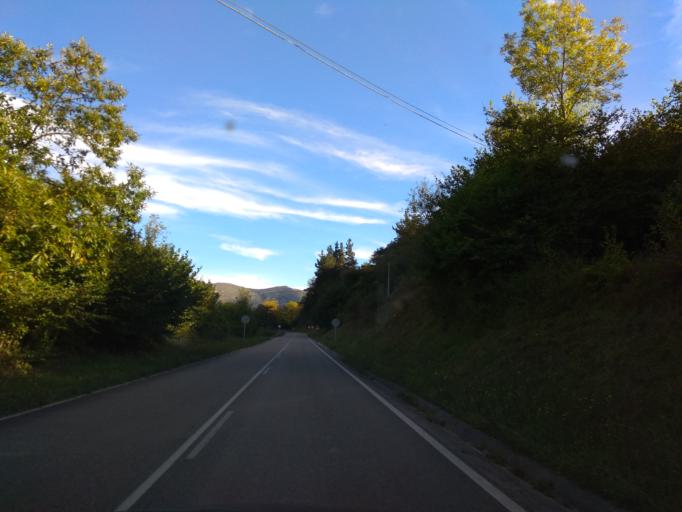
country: ES
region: Cantabria
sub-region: Provincia de Cantabria
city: Ruente
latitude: 43.2196
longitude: -4.3846
